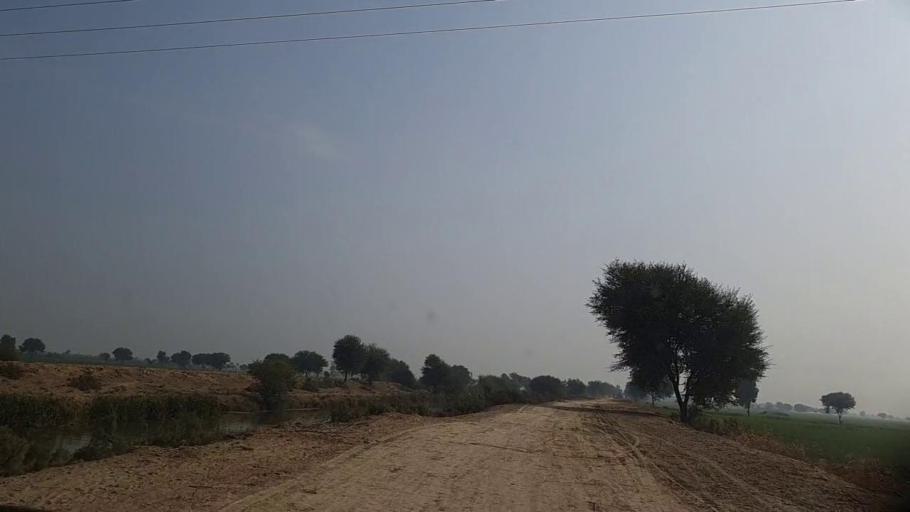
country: PK
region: Sindh
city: Sanghar
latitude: 26.0476
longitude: 68.9872
